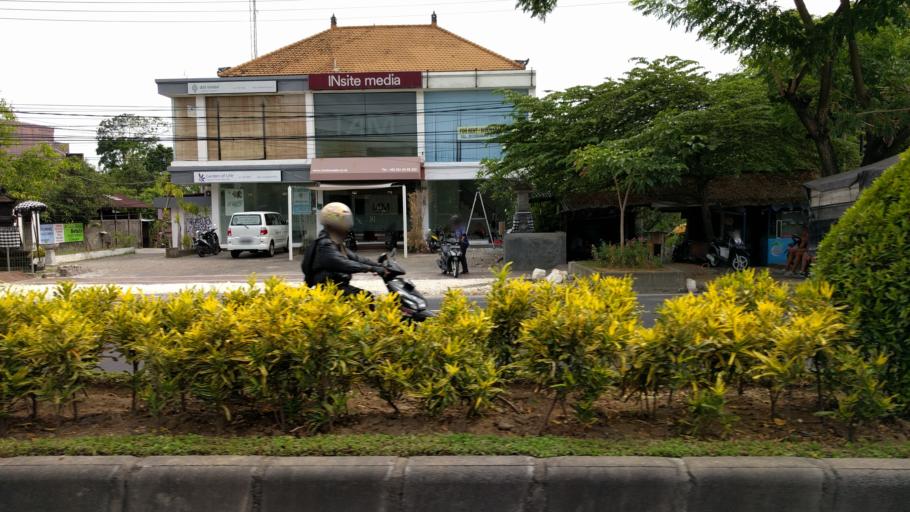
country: ID
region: Bali
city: Kuta
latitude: -8.6839
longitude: 115.1683
